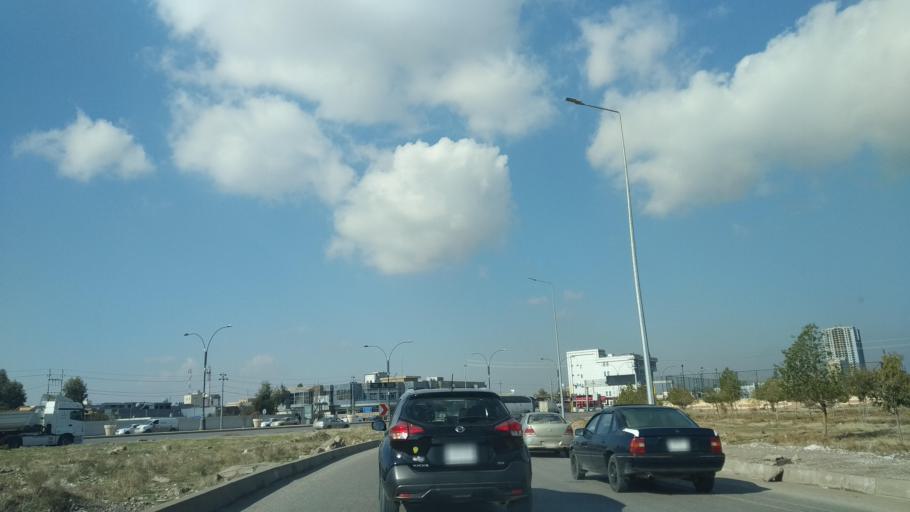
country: IQ
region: Arbil
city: Erbil
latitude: 36.1384
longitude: 44.0220
